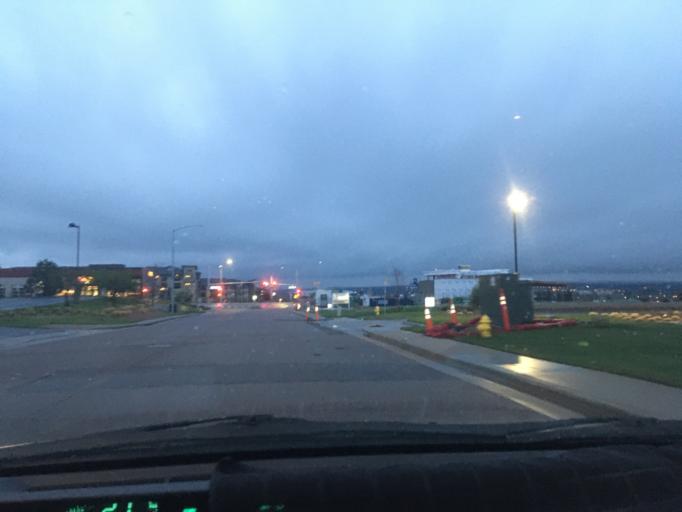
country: US
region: Colorado
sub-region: Broomfield County
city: Broomfield
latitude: 39.9061
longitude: -105.0985
